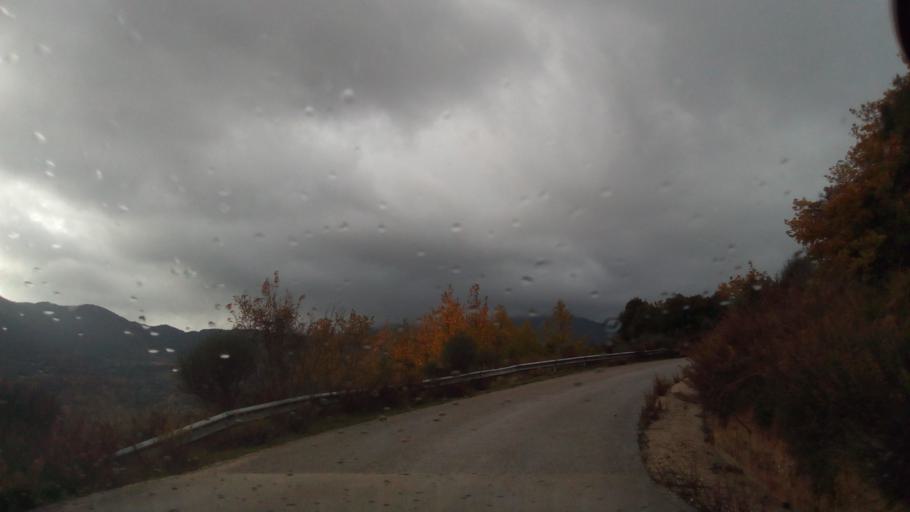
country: GR
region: West Greece
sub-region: Nomos Aitolias kai Akarnanias
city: Thermo
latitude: 38.6741
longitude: 21.8549
